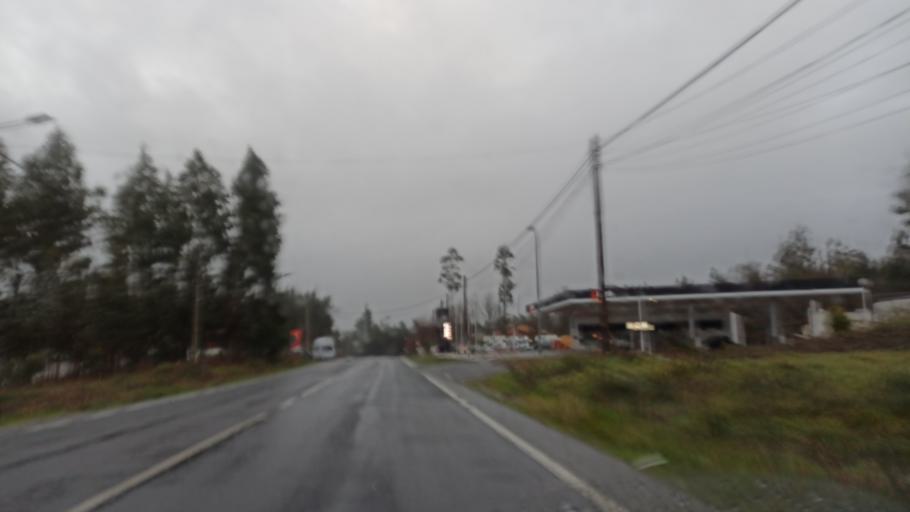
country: ES
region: Galicia
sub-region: Provincia da Coruna
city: Coiros
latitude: 43.2252
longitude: -8.1910
